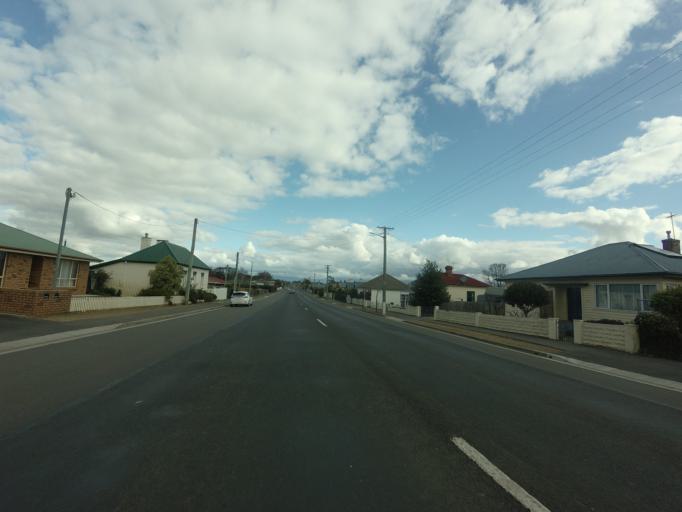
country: AU
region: Tasmania
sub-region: Northern Midlands
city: Longford
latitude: -41.5985
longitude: 147.1209
